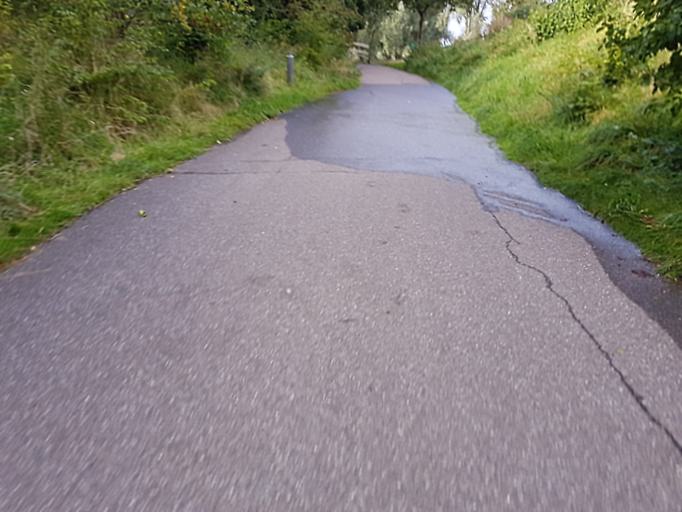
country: DK
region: Capital Region
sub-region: Egedal Kommune
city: Stenlose
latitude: 55.7711
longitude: 12.1747
